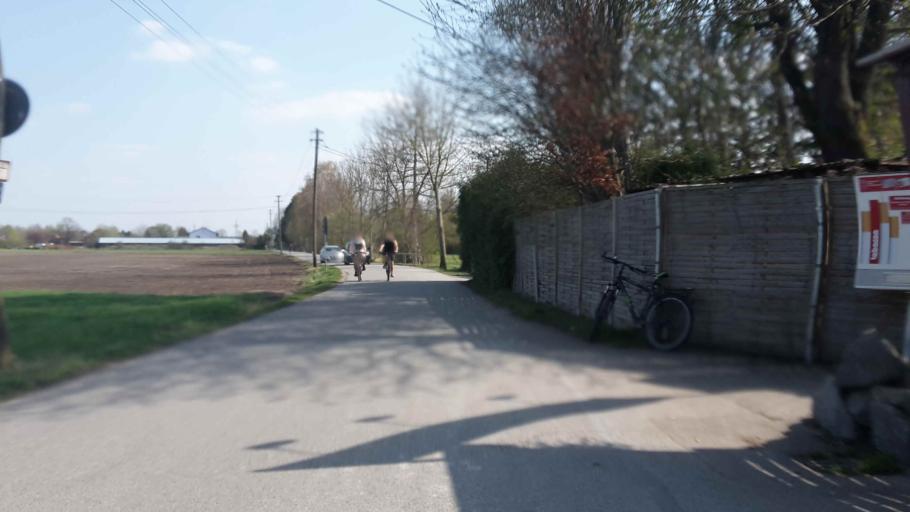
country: DE
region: Bavaria
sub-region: Upper Bavaria
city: Karlsfeld
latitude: 48.1917
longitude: 11.4218
